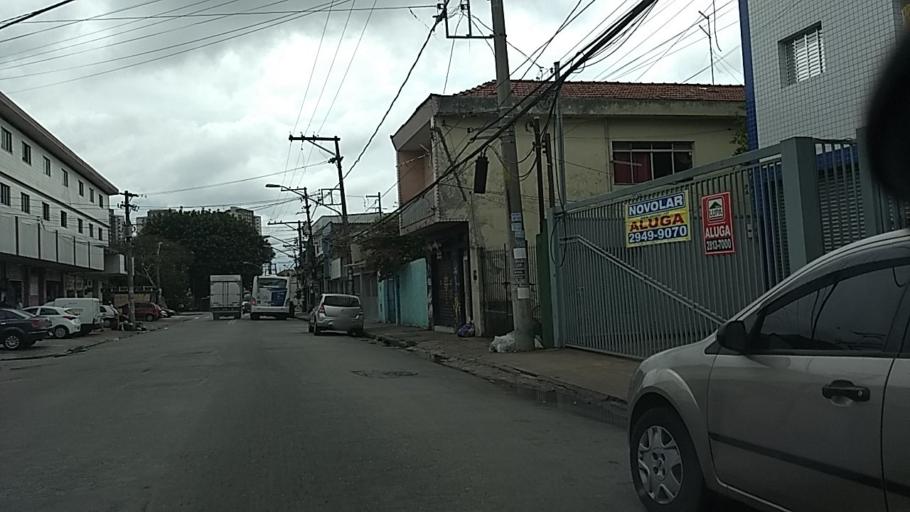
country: BR
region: Sao Paulo
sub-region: Guarulhos
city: Guarulhos
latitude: -23.4880
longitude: -46.5688
